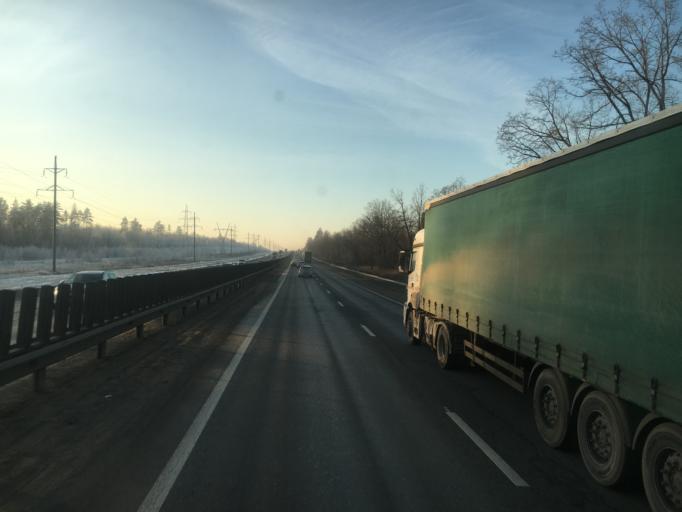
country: RU
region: Samara
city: Pribrezhnyy
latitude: 53.5150
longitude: 49.8812
